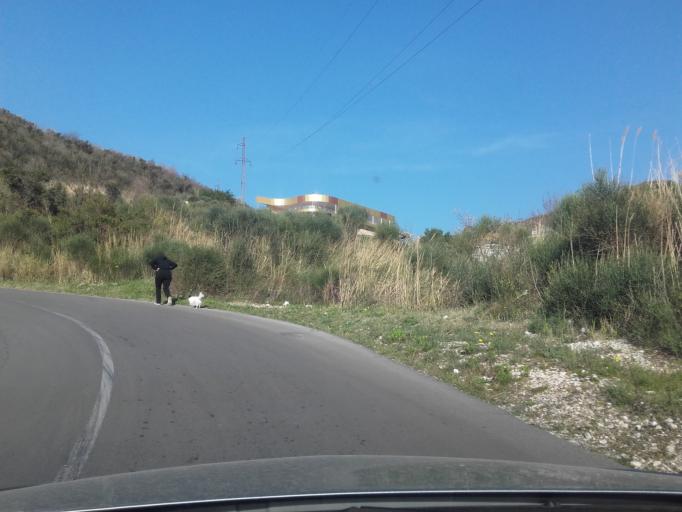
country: ME
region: Budva
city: Budva
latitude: 42.2919
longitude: 18.8247
